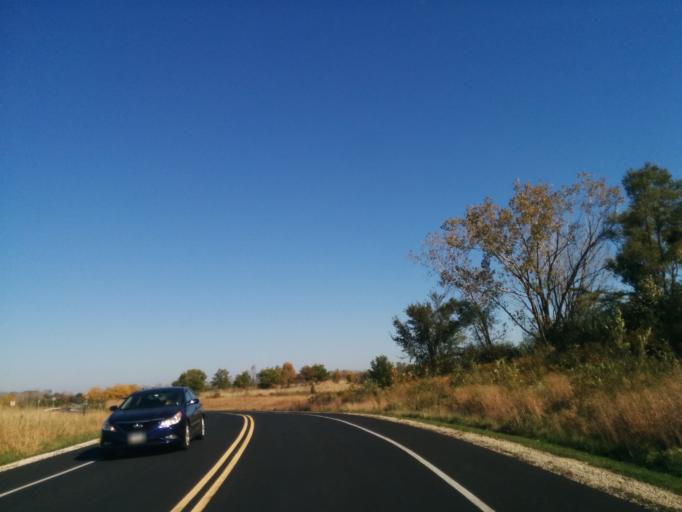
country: US
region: Illinois
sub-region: DuPage County
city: Hanover Park
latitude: 41.9594
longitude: -88.1278
